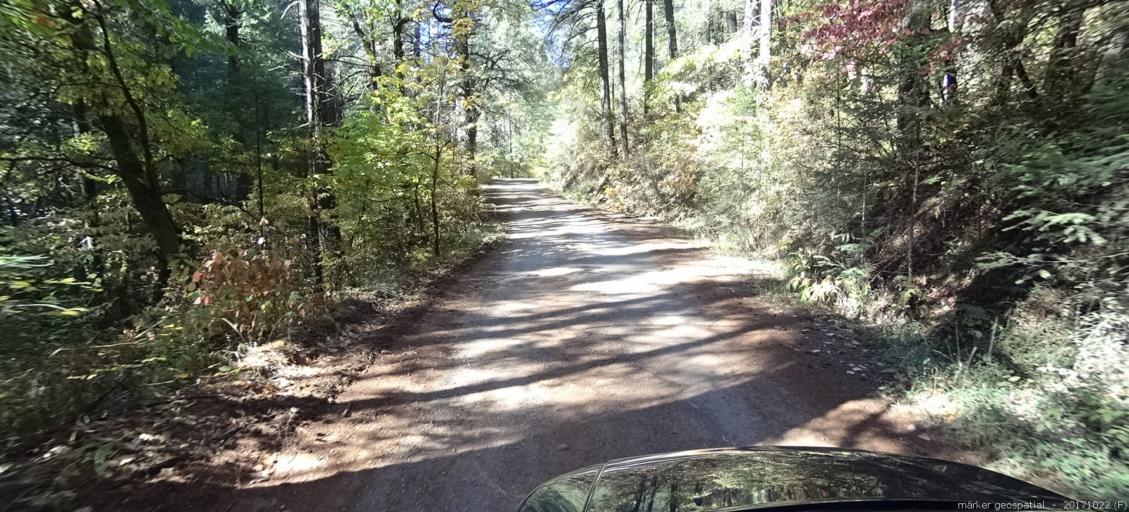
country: US
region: California
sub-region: Shasta County
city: Central Valley (historical)
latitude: 40.9311
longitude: -122.4923
